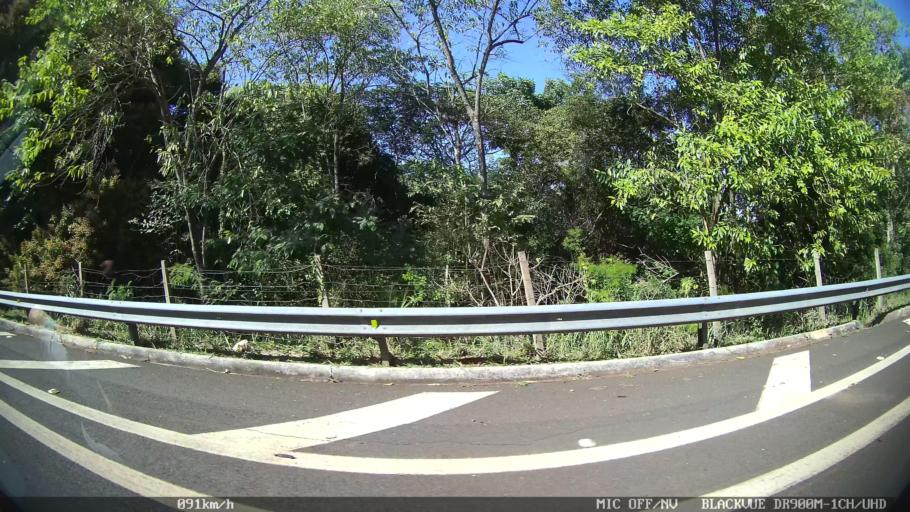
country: BR
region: Sao Paulo
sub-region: Batatais
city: Batatais
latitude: -20.7272
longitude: -47.5185
